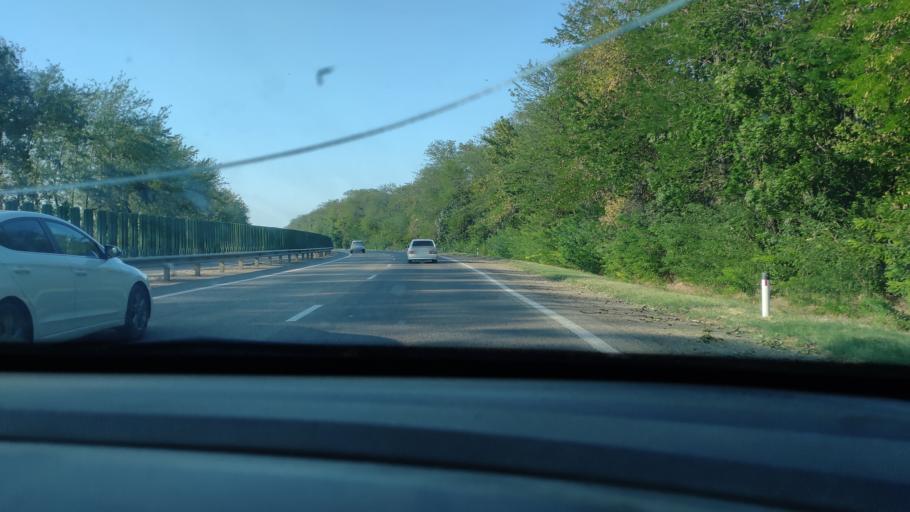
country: RU
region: Krasnodarskiy
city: Timashevsk
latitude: 45.5269
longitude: 38.9417
